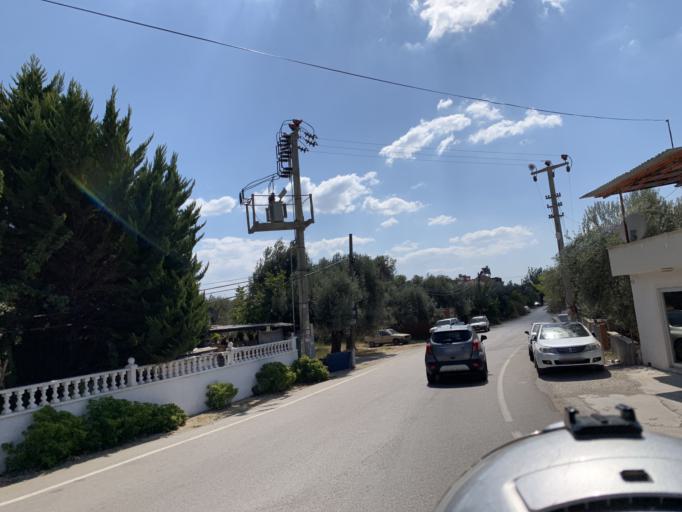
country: TR
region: Balikesir
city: Altinoluk
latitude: 39.5700
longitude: 26.8355
